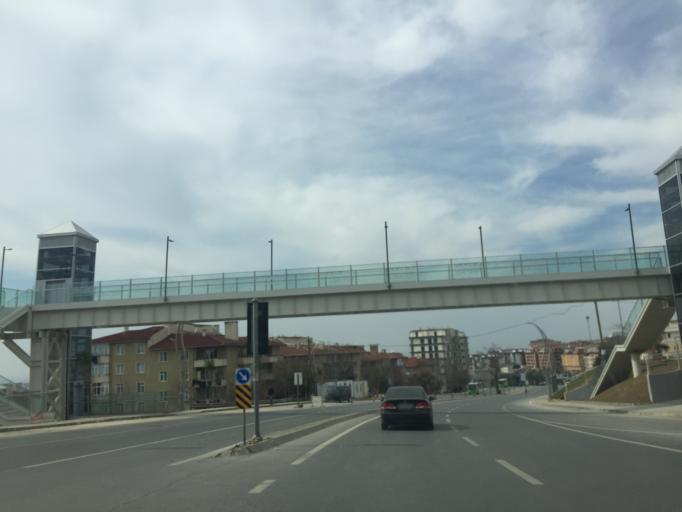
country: TR
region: Kocaeli
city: Gebze
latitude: 40.7890
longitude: 29.4172
